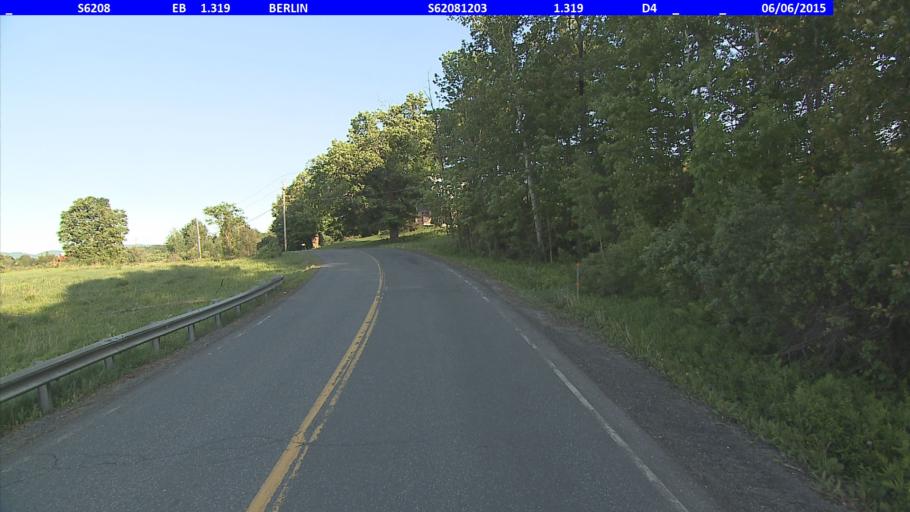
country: US
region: Vermont
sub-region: Washington County
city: South Barre
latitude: 44.1965
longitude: -72.5658
